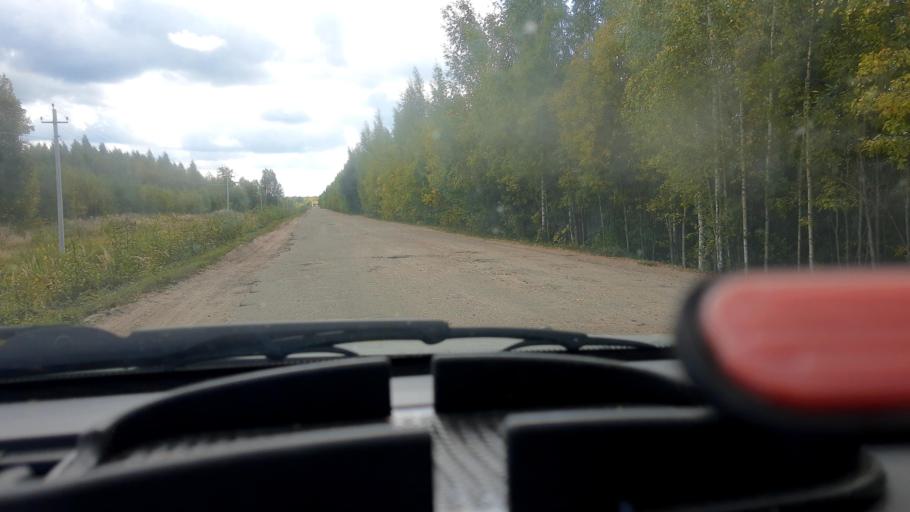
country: RU
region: Mariy-El
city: Kilemary
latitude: 56.8925
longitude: 46.7537
